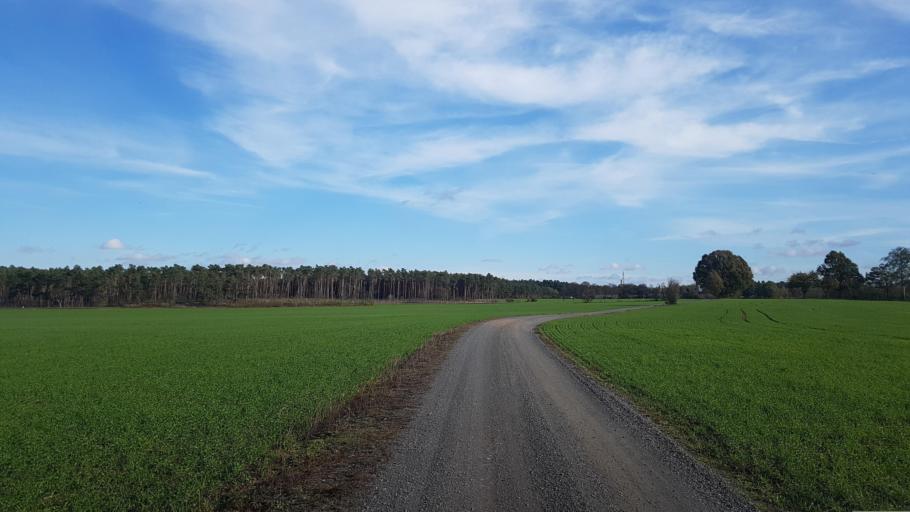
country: DE
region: Brandenburg
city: Schlieben
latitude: 51.7374
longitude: 13.3683
